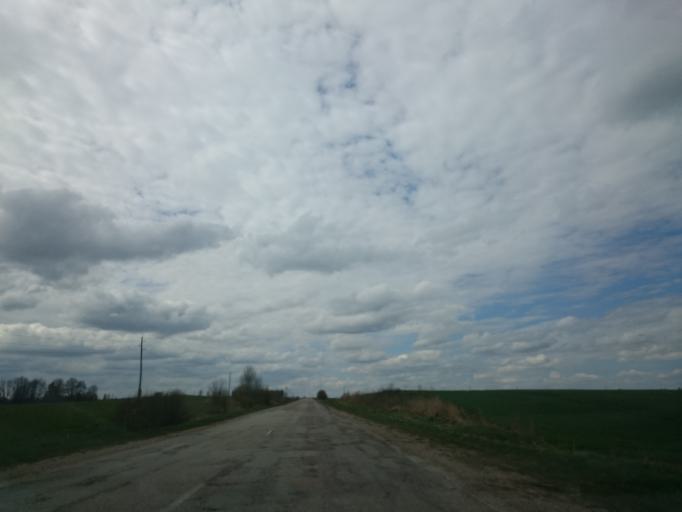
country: LV
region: Jaunpils
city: Jaunpils
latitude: 56.9090
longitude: 22.9519
